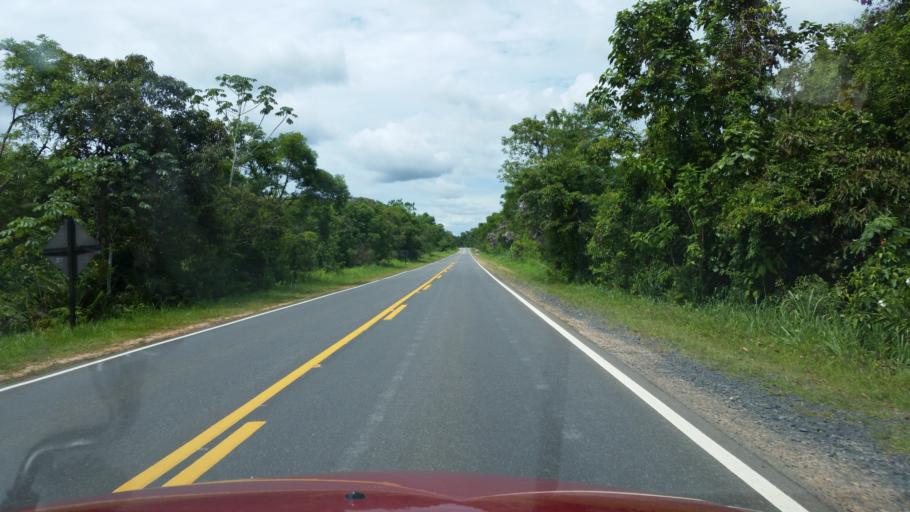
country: BR
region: Sao Paulo
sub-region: Juquia
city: Juquia
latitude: -24.4014
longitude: -47.5283
